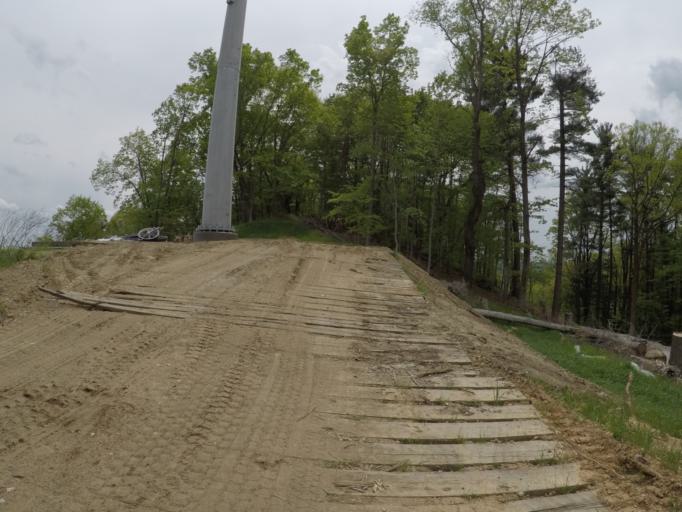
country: US
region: West Virginia
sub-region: Cabell County
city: Huntington
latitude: 38.4195
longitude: -82.3933
